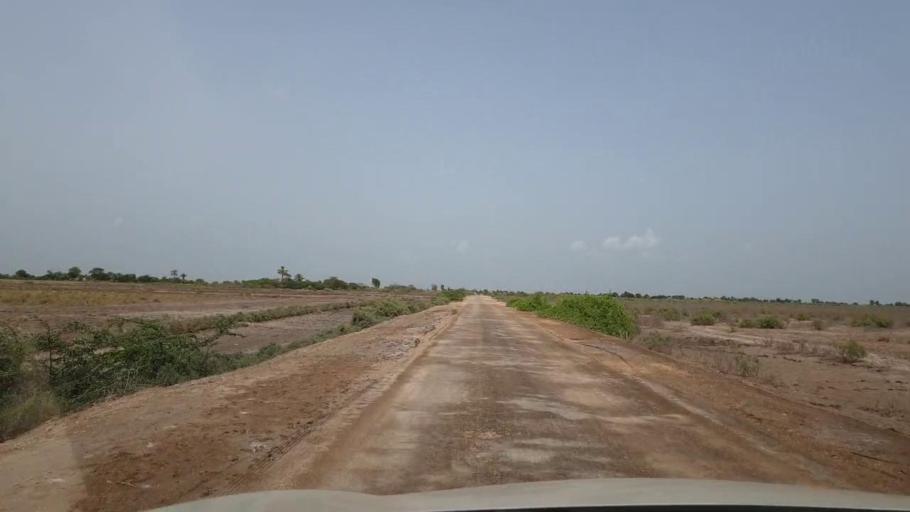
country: PK
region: Sindh
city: Mirwah Gorchani
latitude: 25.2560
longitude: 68.9530
